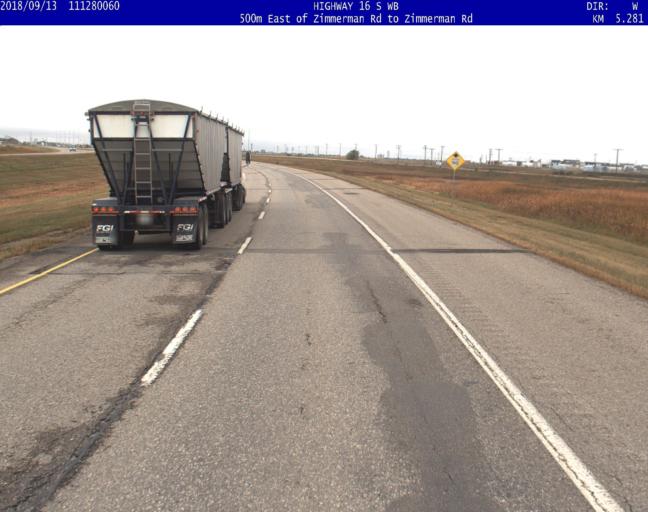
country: CA
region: Saskatchewan
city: Saskatoon
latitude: 52.0857
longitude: -106.5216
